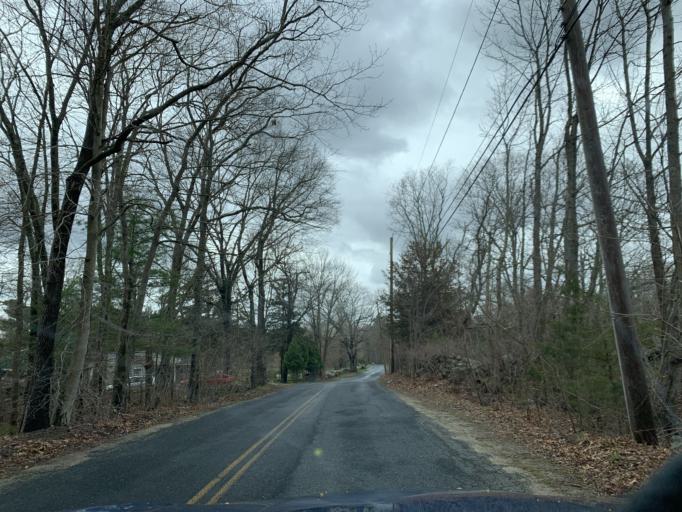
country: US
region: Massachusetts
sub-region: Bristol County
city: Rehoboth
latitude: 41.8854
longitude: -71.2082
